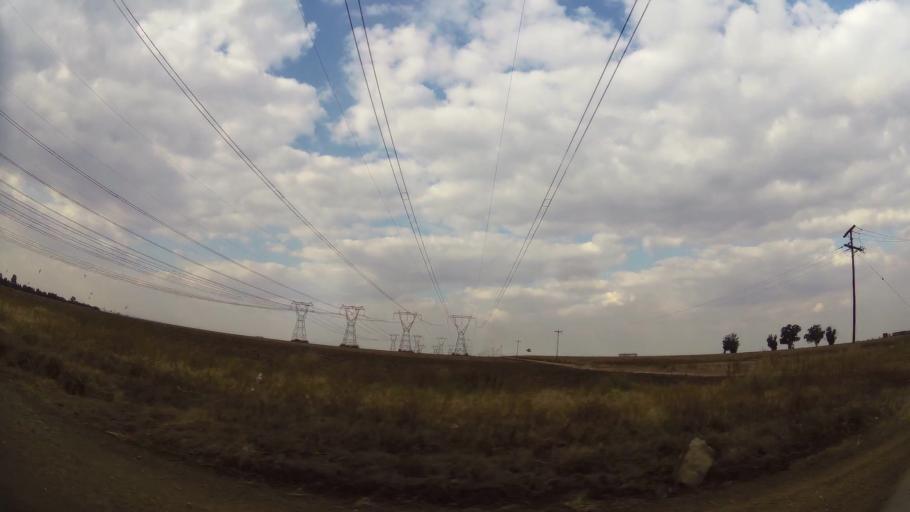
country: ZA
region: Mpumalanga
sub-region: Nkangala District Municipality
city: Delmas
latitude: -26.2522
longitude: 28.6336
